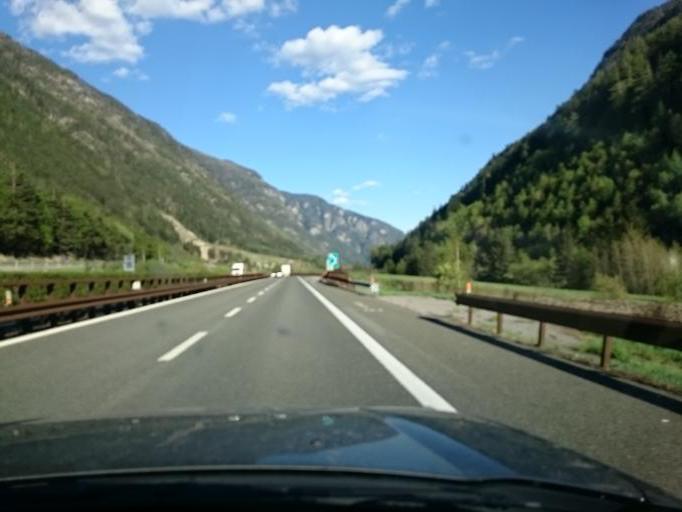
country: IT
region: Trentino-Alto Adige
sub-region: Bolzano
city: Fortezza
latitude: 46.8134
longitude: 11.5497
